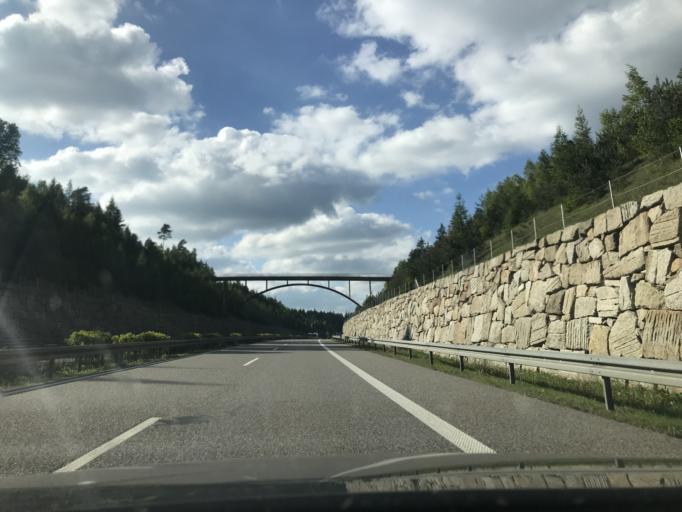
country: DE
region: Thuringia
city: Sankt Kilian
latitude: 50.5269
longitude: 10.7480
